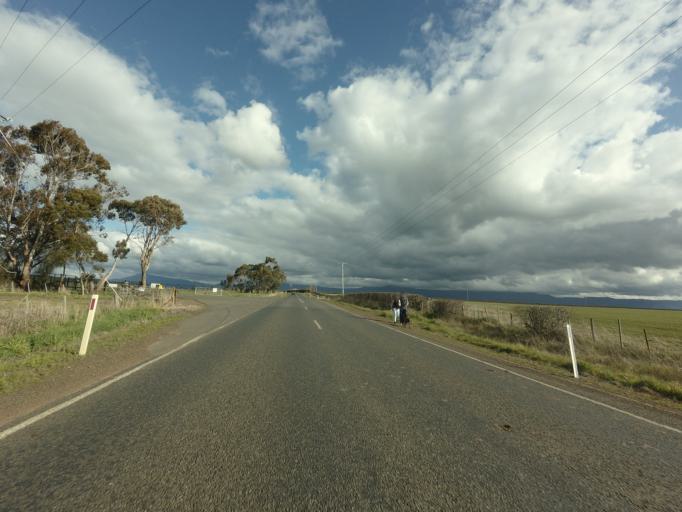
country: AU
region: Tasmania
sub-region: Northern Midlands
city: Longford
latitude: -41.7003
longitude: 147.0772
